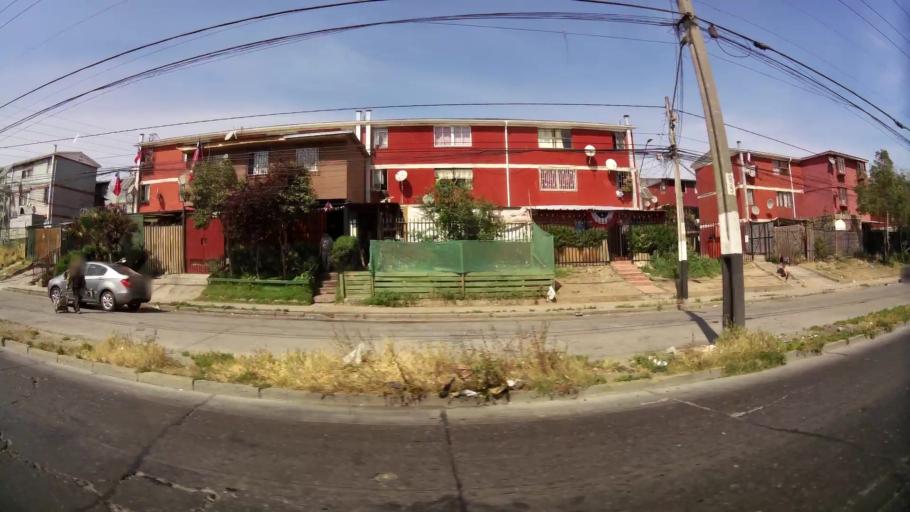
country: CL
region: Santiago Metropolitan
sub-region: Provincia de Santiago
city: Lo Prado
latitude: -33.4446
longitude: -70.7319
